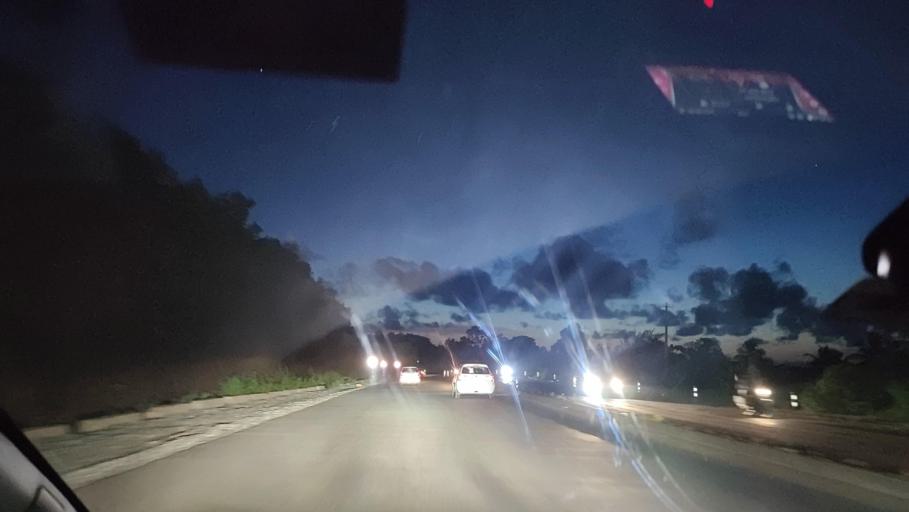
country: IN
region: Karnataka
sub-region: Uttar Kannada
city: Kumta
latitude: 14.4423
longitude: 74.4423
